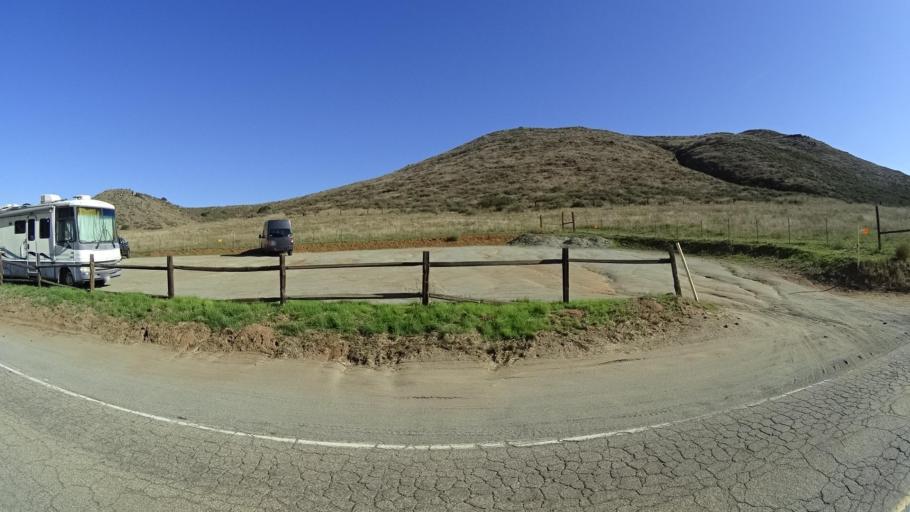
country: US
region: California
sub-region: San Diego County
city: Jamul
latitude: 32.6703
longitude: -116.8229
